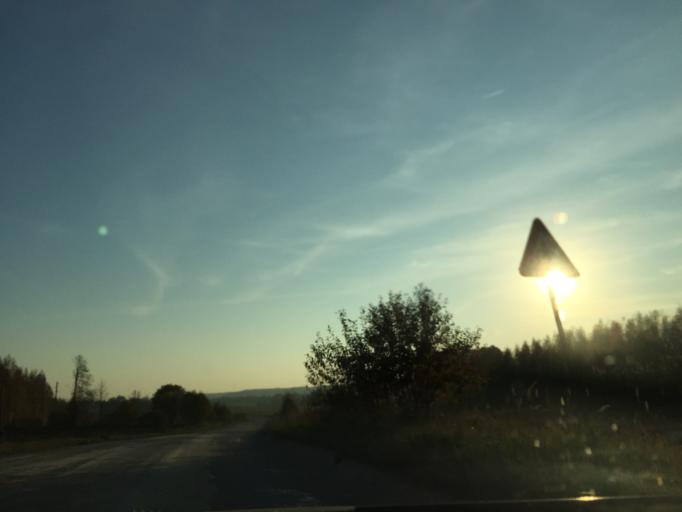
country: LV
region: Vainode
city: Vainode
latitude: 56.5350
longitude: 21.8330
